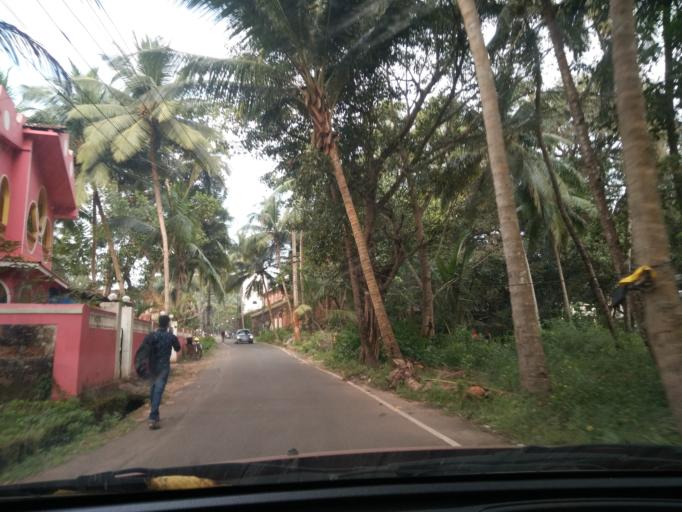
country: IN
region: Goa
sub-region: South Goa
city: Varca
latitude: 15.2318
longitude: 73.9451
